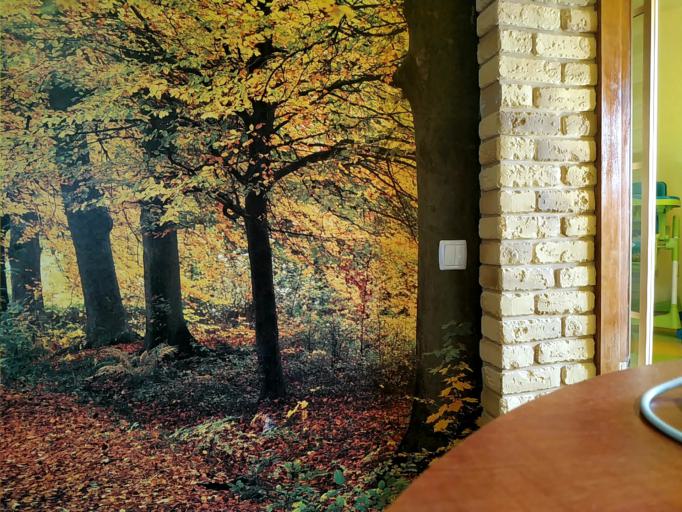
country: RU
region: Tverskaya
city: Kalashnikovo
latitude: 57.3356
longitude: 35.3193
